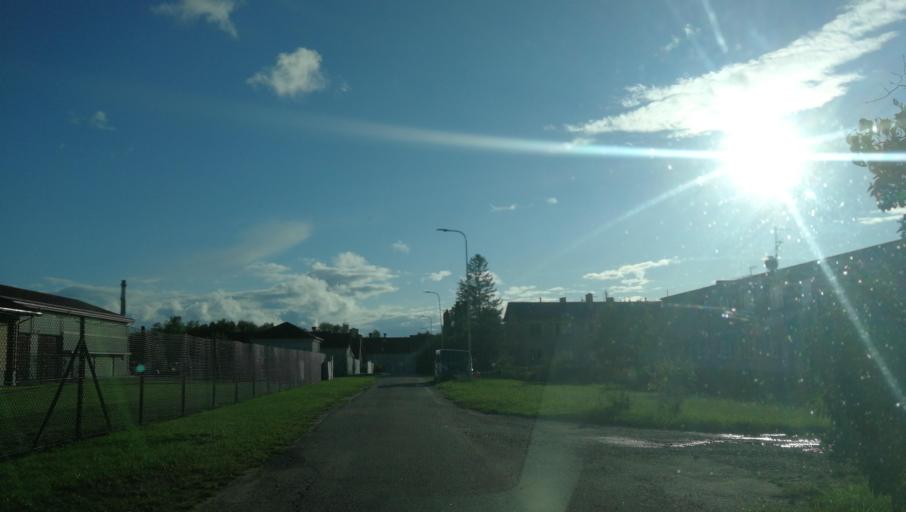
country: LV
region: Valmieras Rajons
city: Valmiera
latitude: 57.5289
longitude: 25.4621
